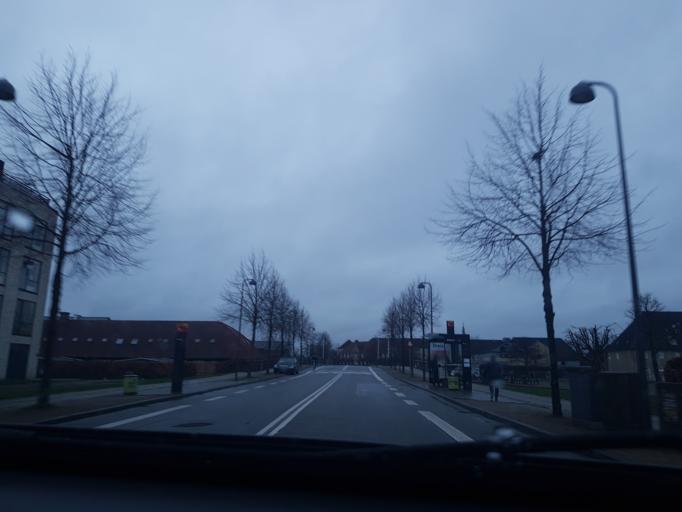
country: DK
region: Capital Region
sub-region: Kobenhavn
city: Christianshavn
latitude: 55.6797
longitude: 12.6034
